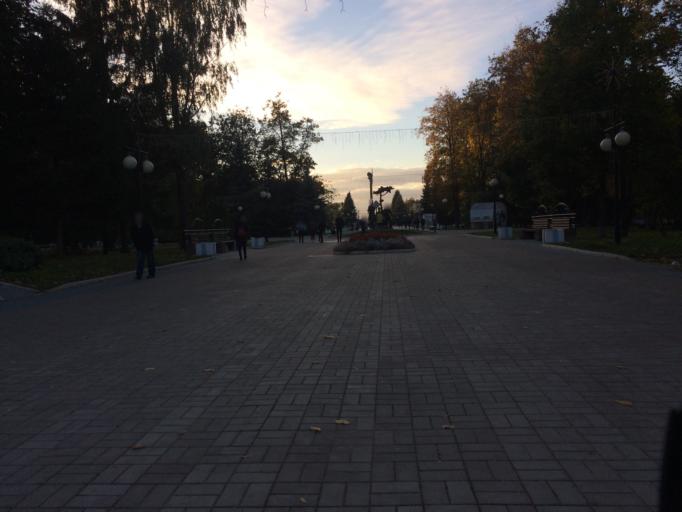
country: RU
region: Mariy-El
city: Yoshkar-Ola
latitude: 56.6361
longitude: 47.8920
